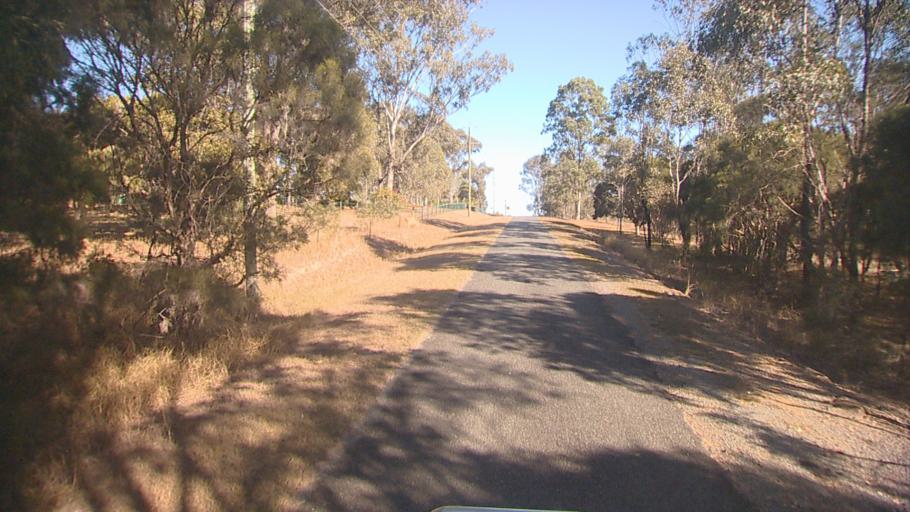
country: AU
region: Queensland
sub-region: Logan
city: Cedar Vale
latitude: -27.8449
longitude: 153.0053
